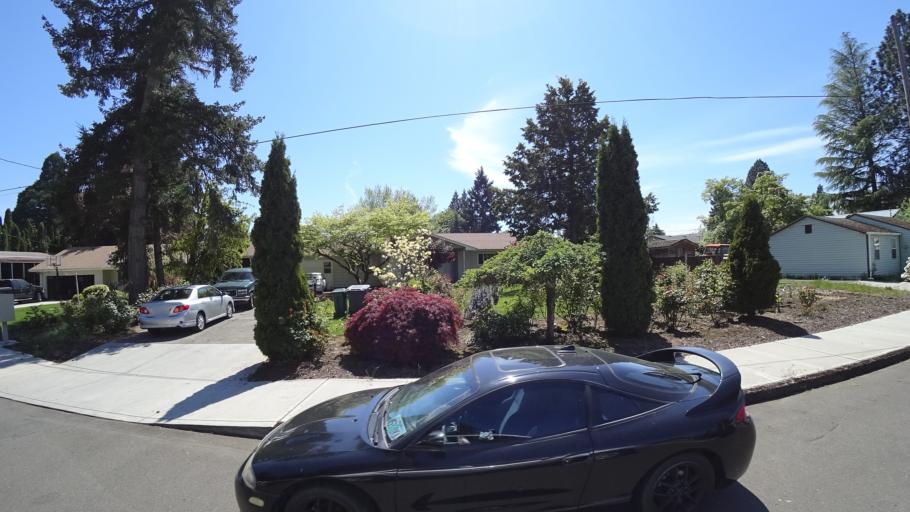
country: US
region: Oregon
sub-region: Washington County
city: Hillsboro
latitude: 45.5135
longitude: -122.9657
